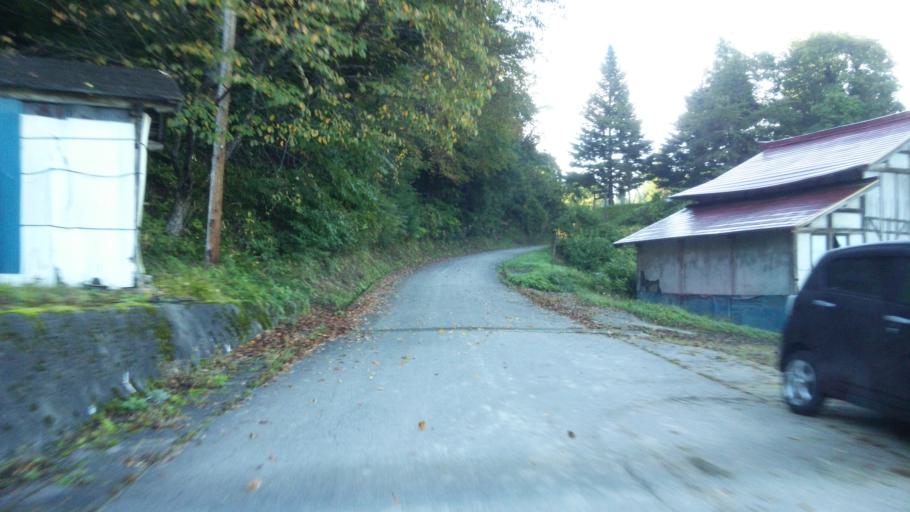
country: JP
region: Fukushima
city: Kitakata
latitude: 37.4505
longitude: 139.7237
